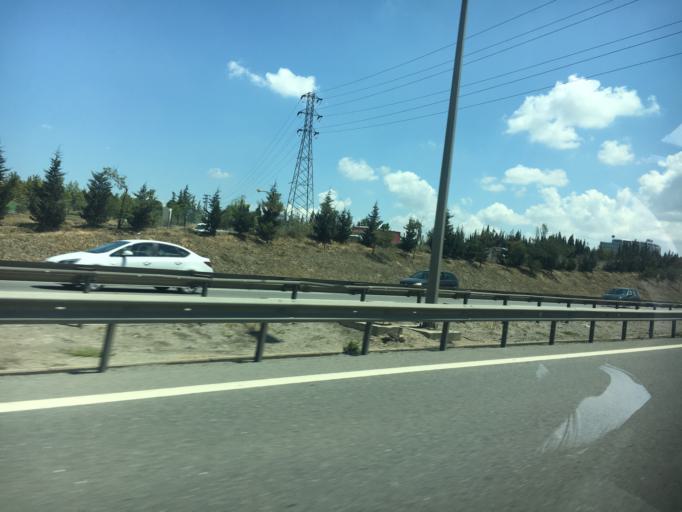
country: TR
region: Kocaeli
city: Balcik
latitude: 40.8890
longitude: 29.3733
